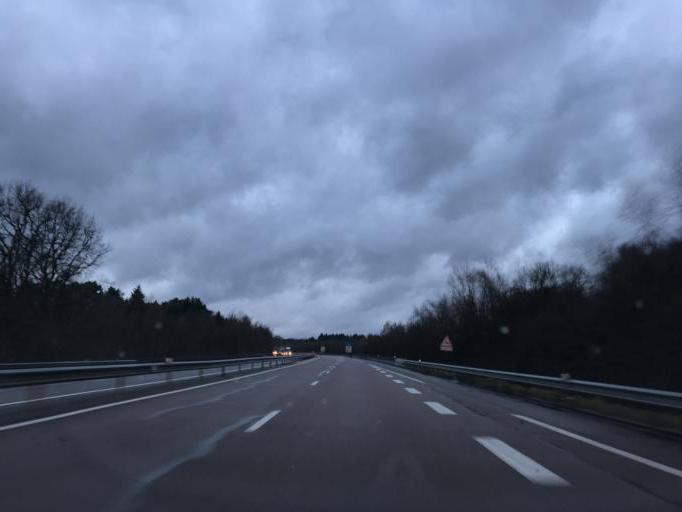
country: FR
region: Franche-Comte
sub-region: Departement du Jura
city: Foucherans
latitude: 47.0712
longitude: 5.4388
